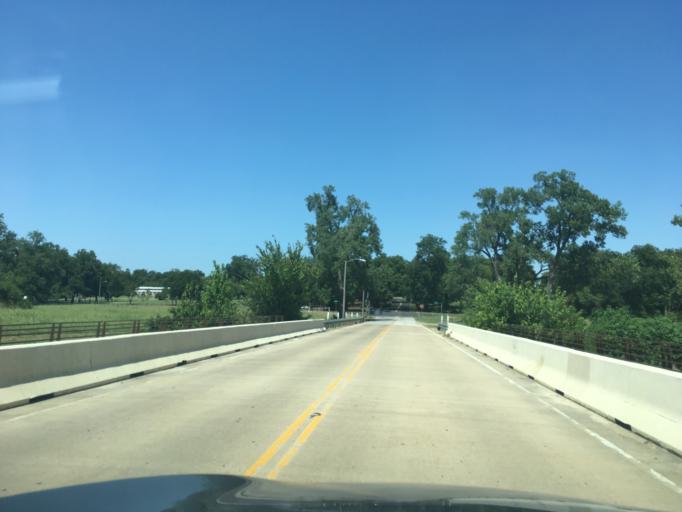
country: US
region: Texas
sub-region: Dallas County
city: Highland Park
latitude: 32.8596
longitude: -96.7300
